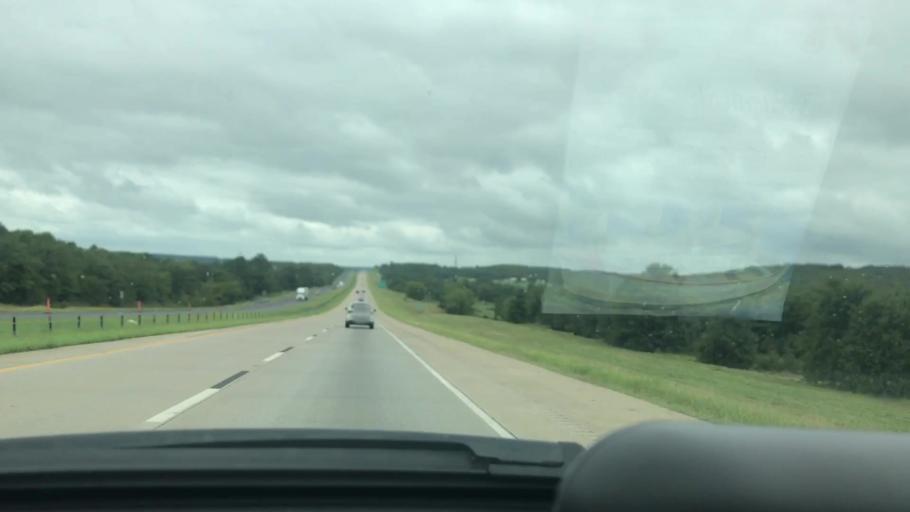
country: US
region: Oklahoma
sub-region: Pittsburg County
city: Krebs
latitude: 34.9739
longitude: -95.7234
